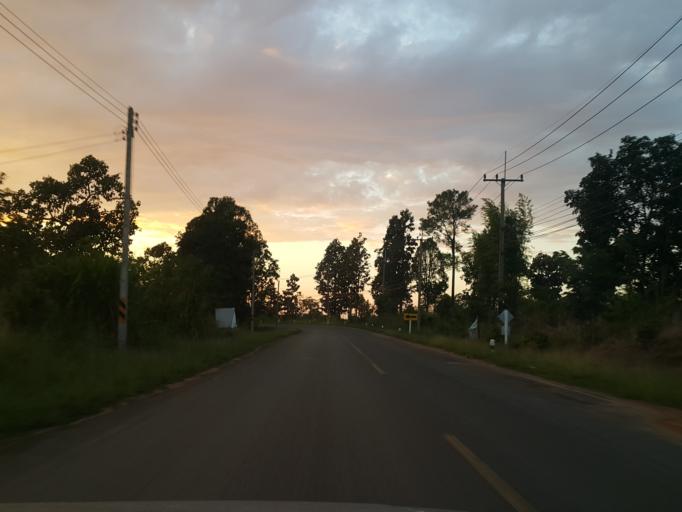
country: TH
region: Mae Hong Son
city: Khun Yuam
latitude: 18.8455
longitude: 97.9614
